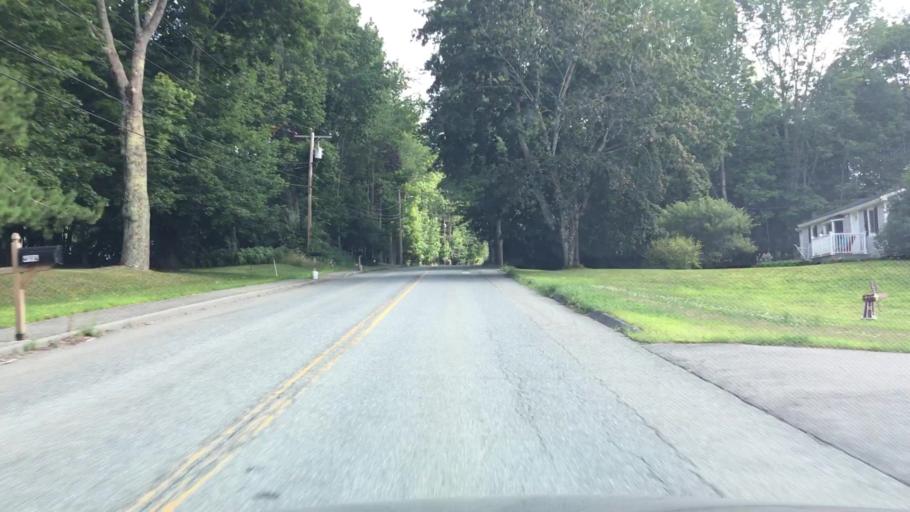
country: US
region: Maine
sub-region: Penobscot County
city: Hampden
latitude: 44.7351
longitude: -68.8598
